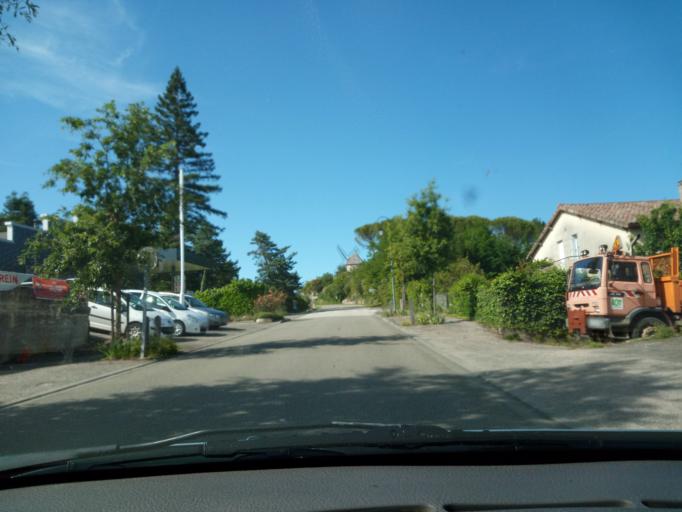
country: FR
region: Midi-Pyrenees
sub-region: Departement du Lot
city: Castelnau-Montratier
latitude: 44.2721
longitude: 1.3537
